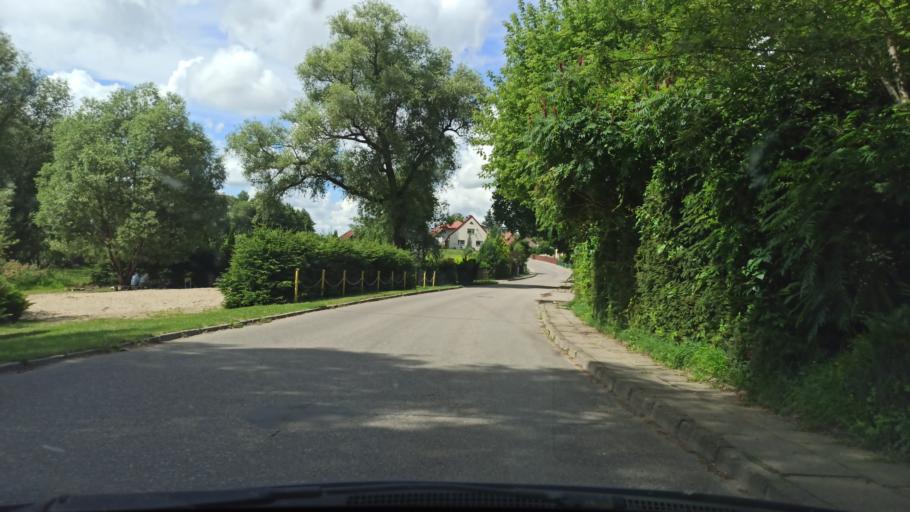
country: PL
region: Warmian-Masurian Voivodeship
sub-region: Powiat ostrodzki
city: Morag
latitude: 53.8644
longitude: 20.0187
